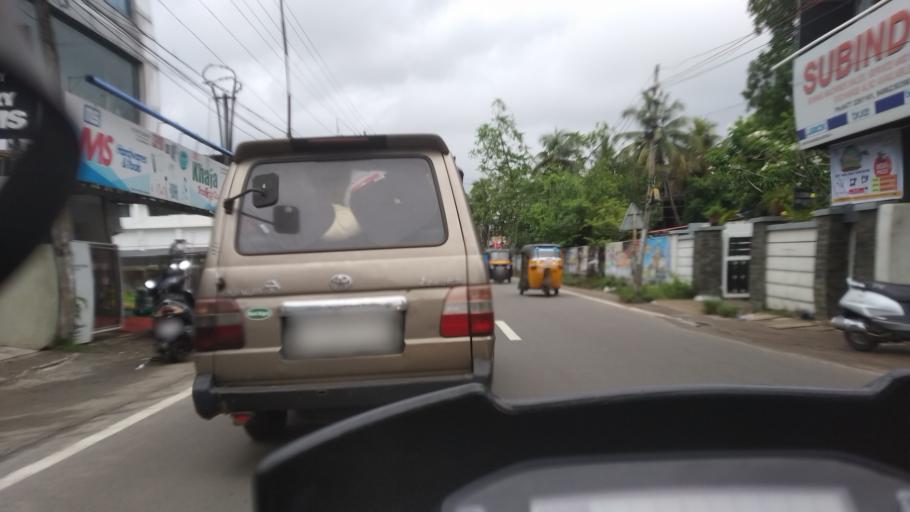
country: IN
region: Kerala
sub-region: Alappuzha
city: Alleppey
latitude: 9.4961
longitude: 76.3389
